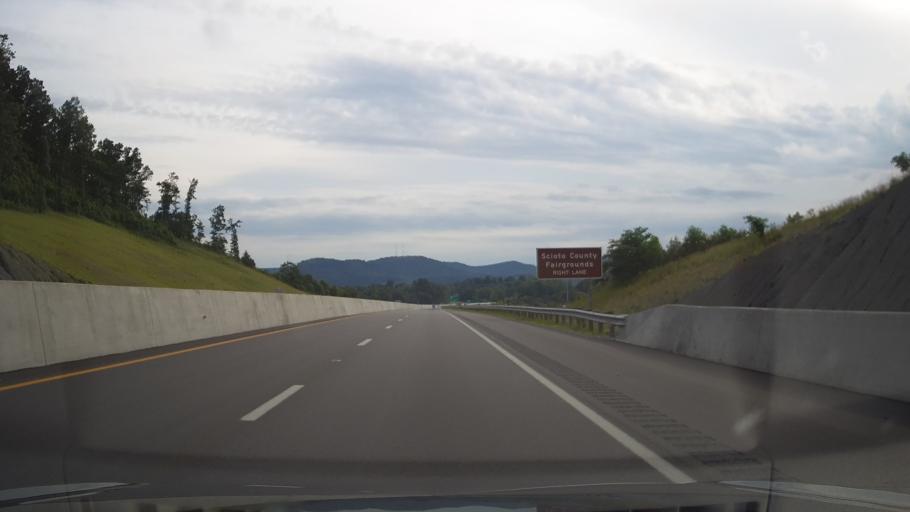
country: US
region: Ohio
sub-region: Scioto County
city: Lucasville
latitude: 38.8952
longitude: -82.9784
